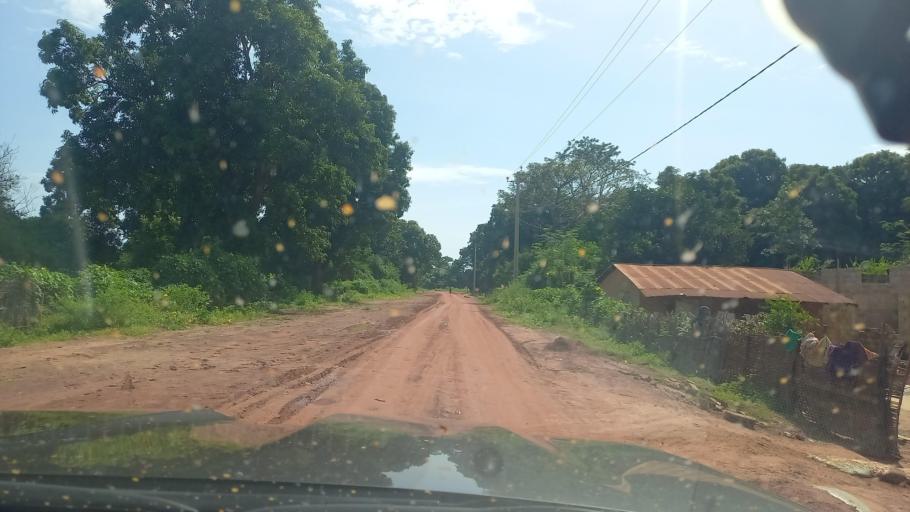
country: SN
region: Ziguinchor
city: Adeane
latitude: 12.6641
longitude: -16.1084
